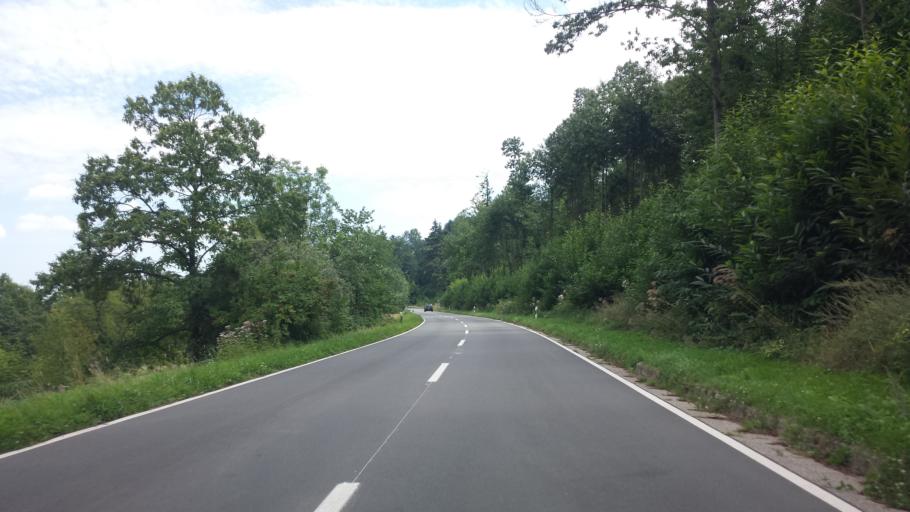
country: DE
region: Rheinland-Pfalz
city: Burrweiler
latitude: 49.2585
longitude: 8.0668
